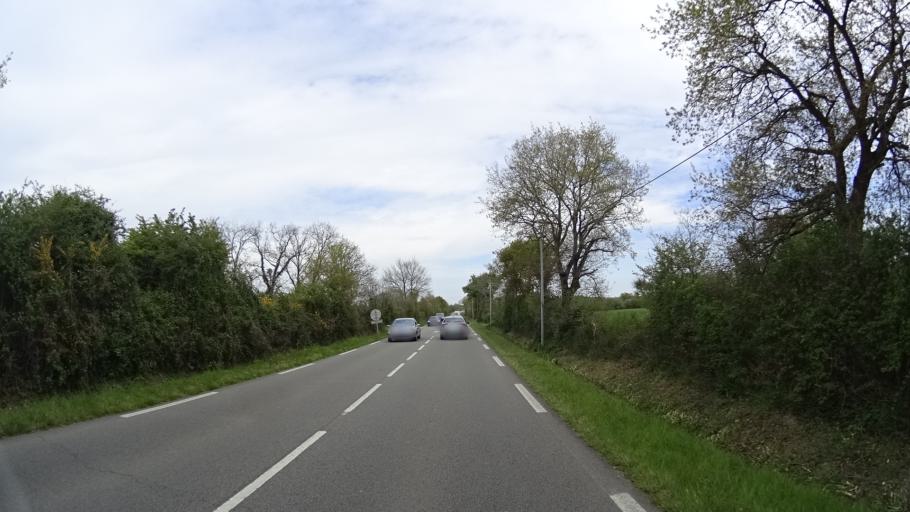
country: FR
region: Pays de la Loire
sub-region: Departement de la Loire-Atlantique
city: Bourgneuf-en-Retz
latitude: 47.0595
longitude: -1.9191
